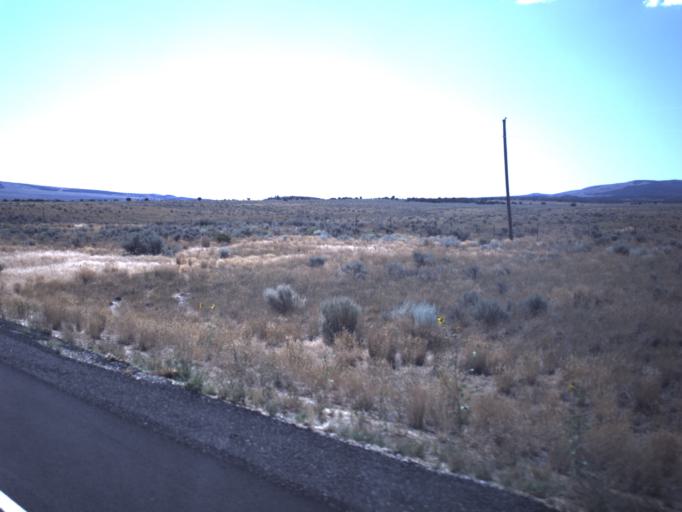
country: US
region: Utah
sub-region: Utah County
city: Eagle Mountain
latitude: 40.0565
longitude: -112.3046
